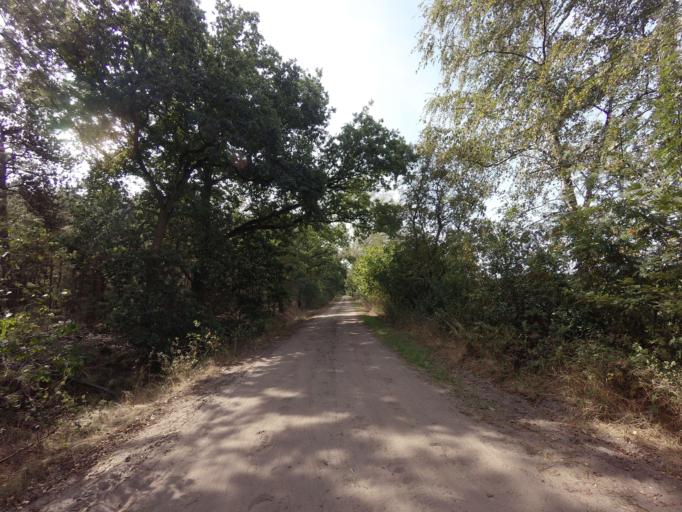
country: NL
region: North Brabant
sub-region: Gemeente Boekel
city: Boekel
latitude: 51.5397
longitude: 5.7561
